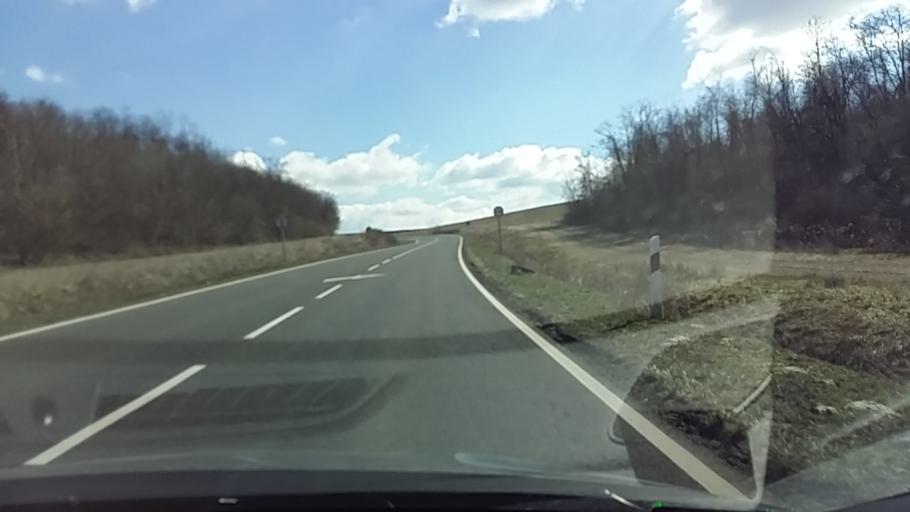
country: HU
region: Baranya
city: Kozarmisleny
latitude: 46.0252
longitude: 18.2801
